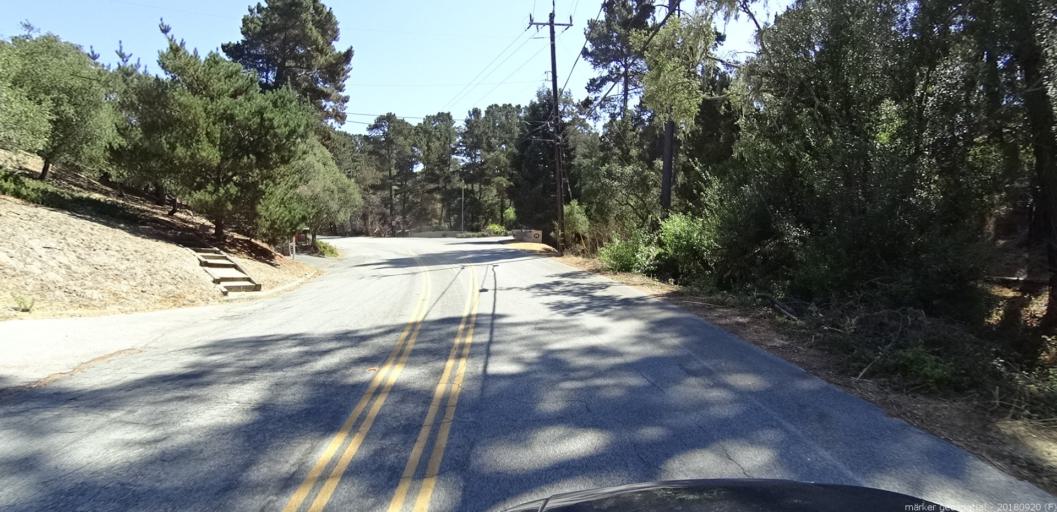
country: US
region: California
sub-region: Monterey County
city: Del Rey Oaks
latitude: 36.5821
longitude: -121.8634
